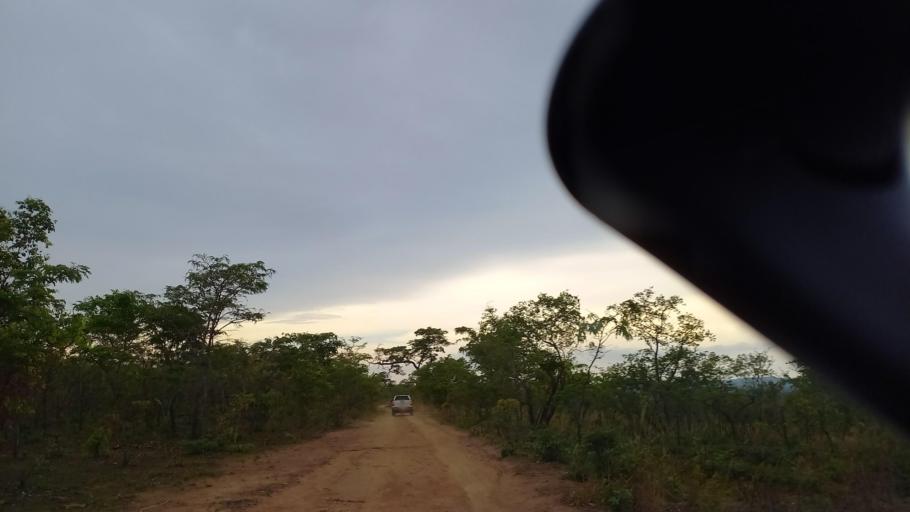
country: ZM
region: Lusaka
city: Kafue
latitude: -16.0508
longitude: 28.3343
